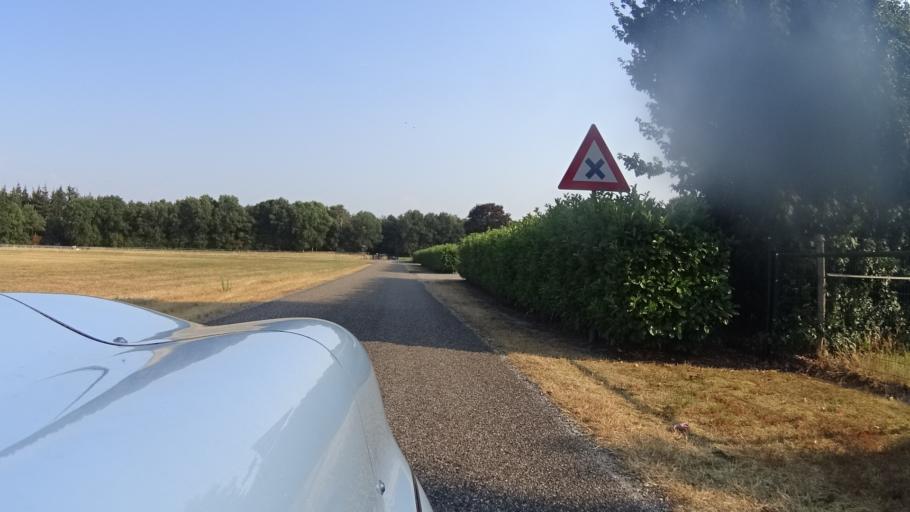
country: NL
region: North Brabant
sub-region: Gemeente Mill en Sint Hubert
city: Wilbertoord
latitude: 51.6841
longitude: 5.7550
